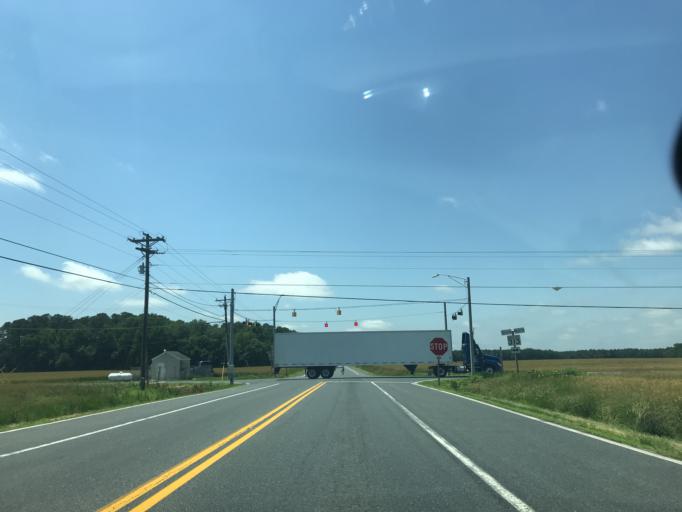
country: US
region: Maryland
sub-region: Caroline County
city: Federalsburg
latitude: 38.6321
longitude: -75.7703
